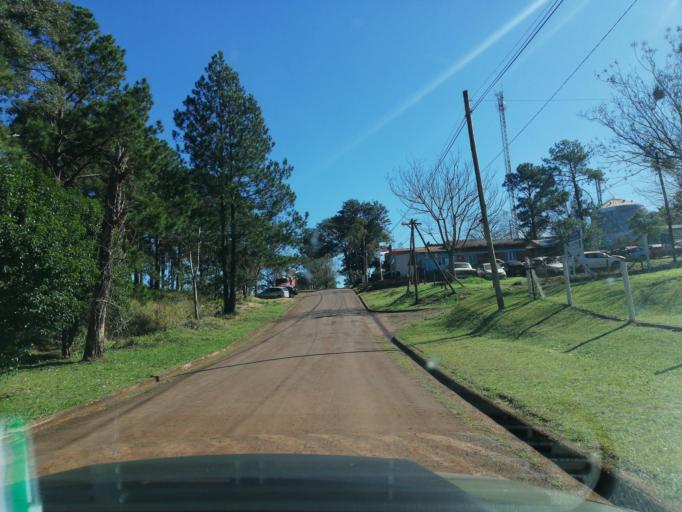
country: AR
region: Misiones
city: Aristobulo del Valle
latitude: -27.0846
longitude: -54.8355
